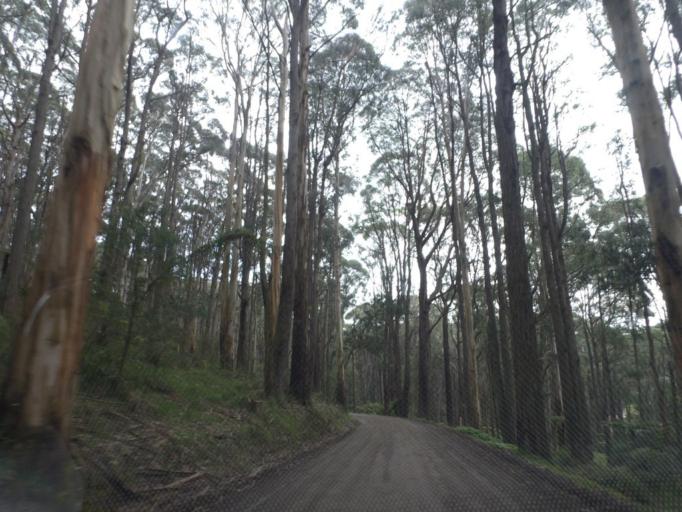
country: AU
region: Victoria
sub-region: Yarra Ranges
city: Olinda
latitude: -37.8572
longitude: 145.3482
